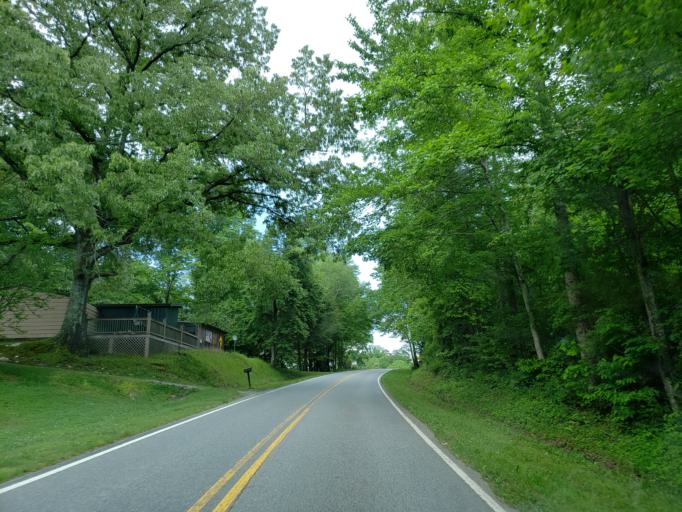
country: US
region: Georgia
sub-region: Fannin County
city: Blue Ridge
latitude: 34.8507
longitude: -84.3874
